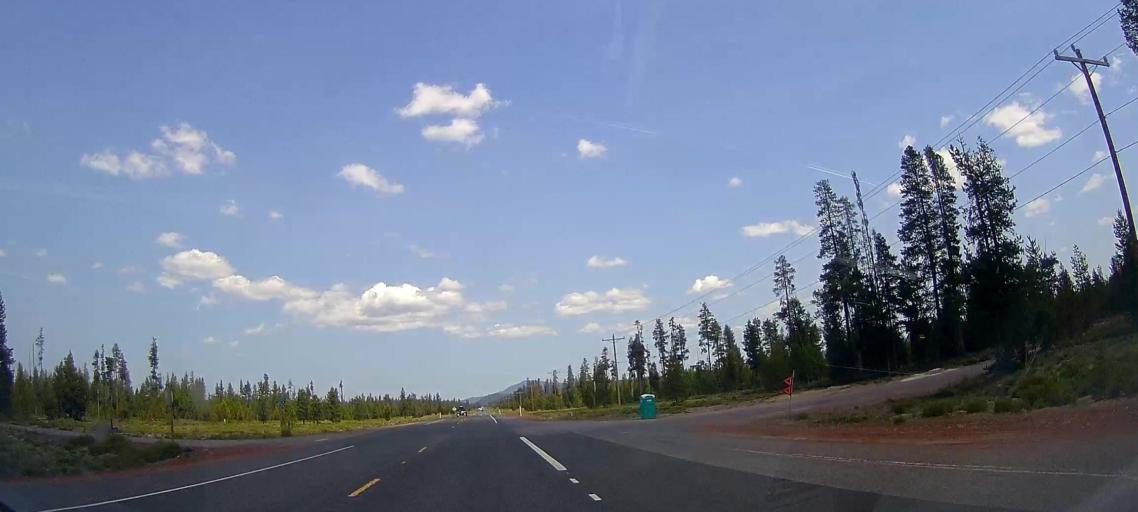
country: US
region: Oregon
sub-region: Deschutes County
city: La Pine
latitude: 43.1535
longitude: -121.7948
